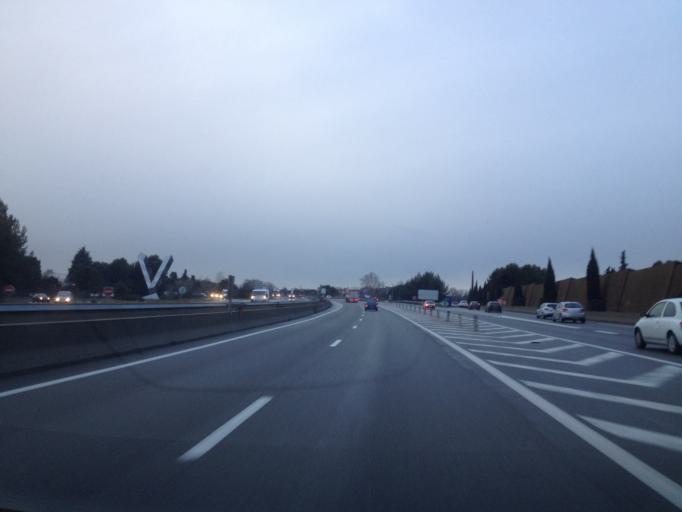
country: FR
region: Provence-Alpes-Cote d'Azur
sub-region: Departement des Bouches-du-Rhone
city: Aix-en-Provence
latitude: 43.5176
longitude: 5.4312
